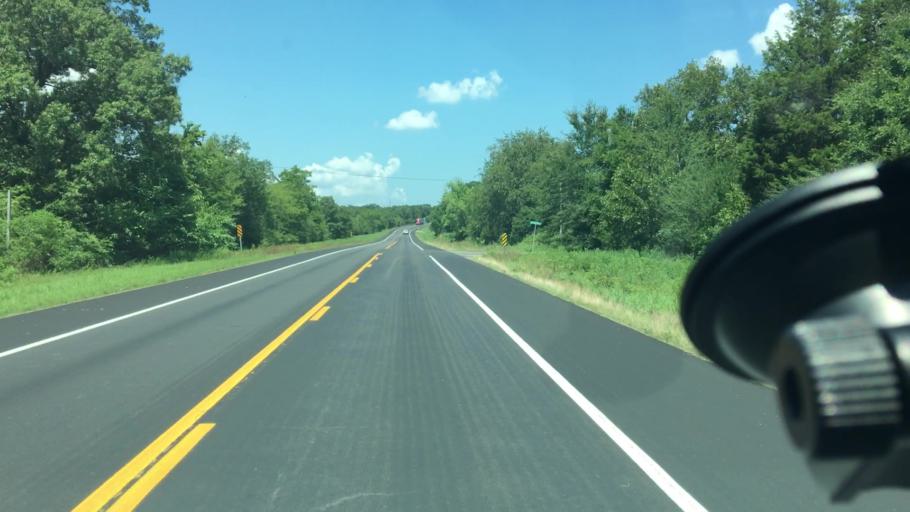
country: US
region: Arkansas
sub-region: Sebastian County
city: Lavaca
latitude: 35.2975
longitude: -94.1512
